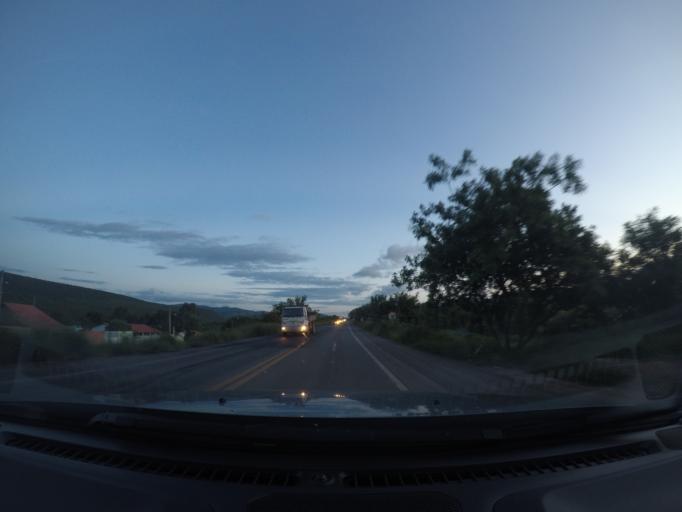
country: BR
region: Bahia
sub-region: Seabra
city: Seabra
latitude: -12.4684
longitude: -41.7432
